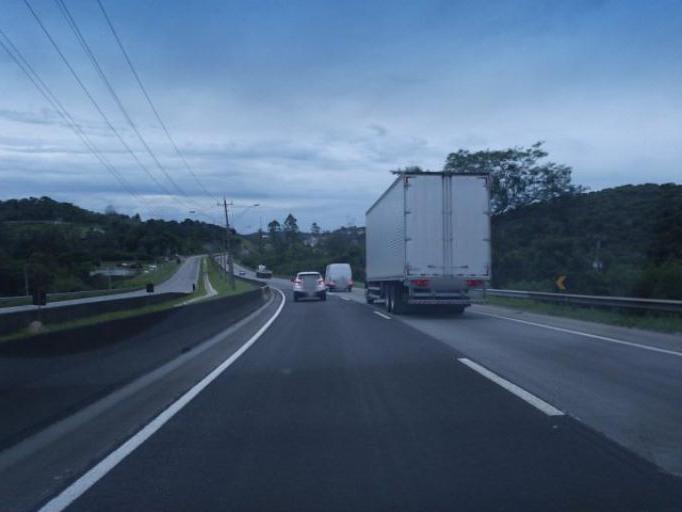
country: BR
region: Sao Paulo
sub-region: Sao Lourenco Da Serra
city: Sao Lourenco da Serra
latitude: -23.8741
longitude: -46.9656
